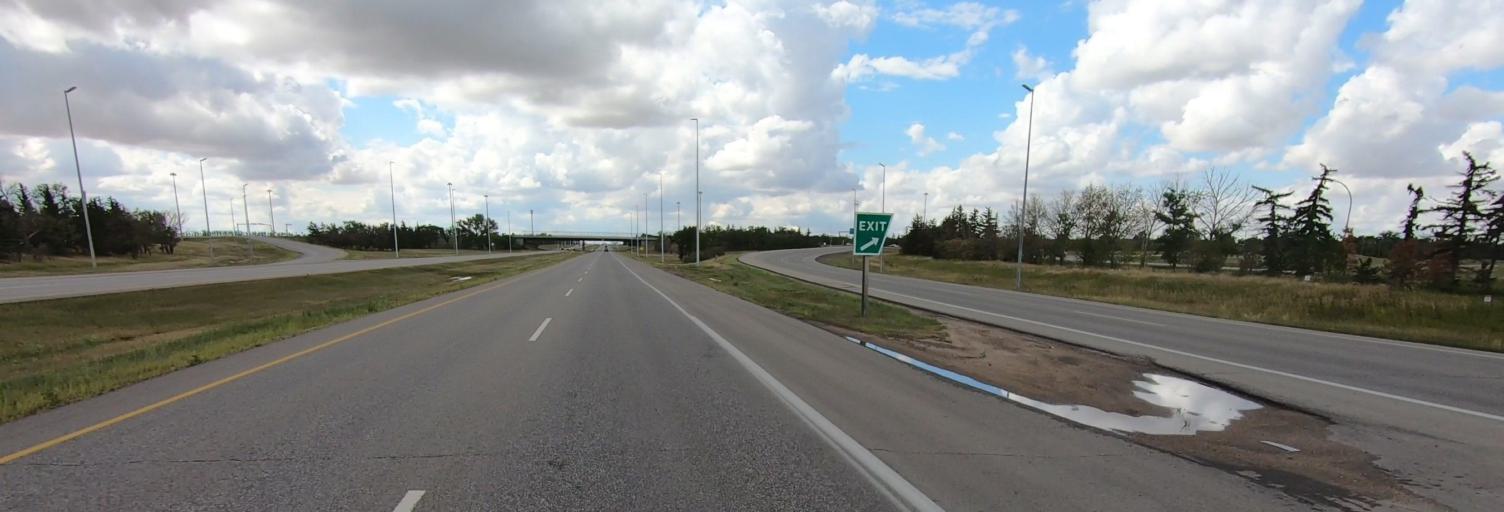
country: CA
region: Saskatchewan
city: Regina
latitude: 50.4116
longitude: -104.5867
